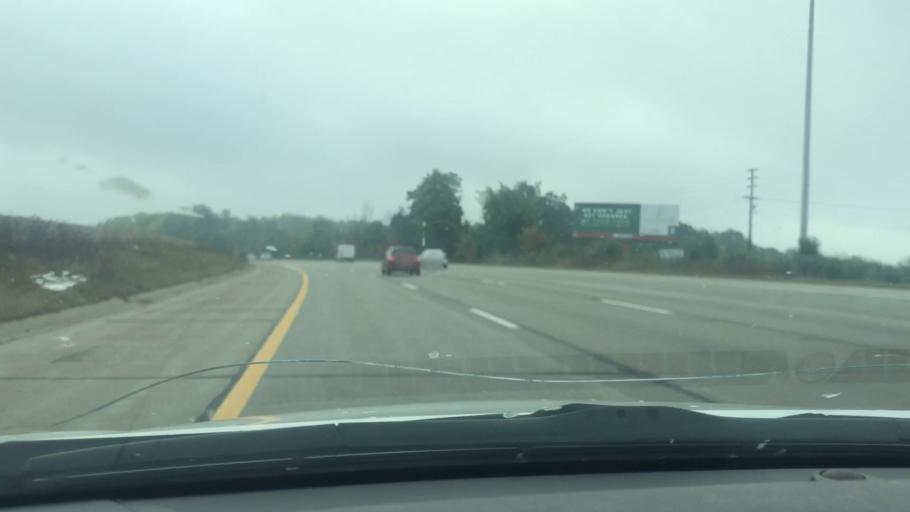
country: US
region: Michigan
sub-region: Livingston County
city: Howell
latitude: 42.5872
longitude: -83.9299
